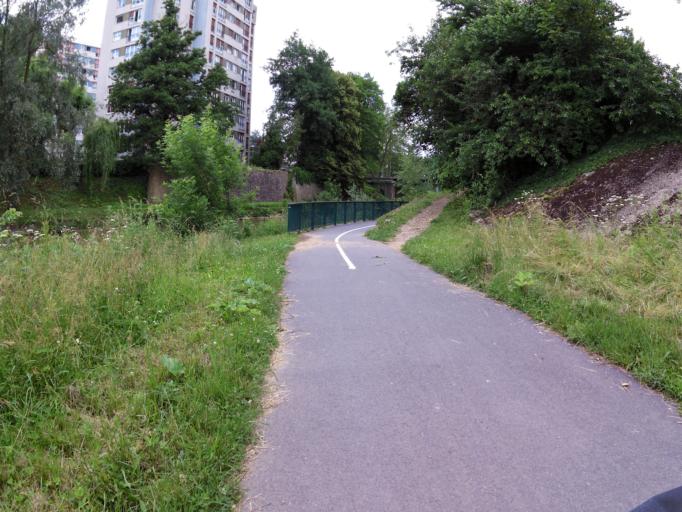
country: FR
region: Champagne-Ardenne
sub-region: Departement des Ardennes
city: Charleville-Mezieres
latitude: 49.7576
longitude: 4.7261
